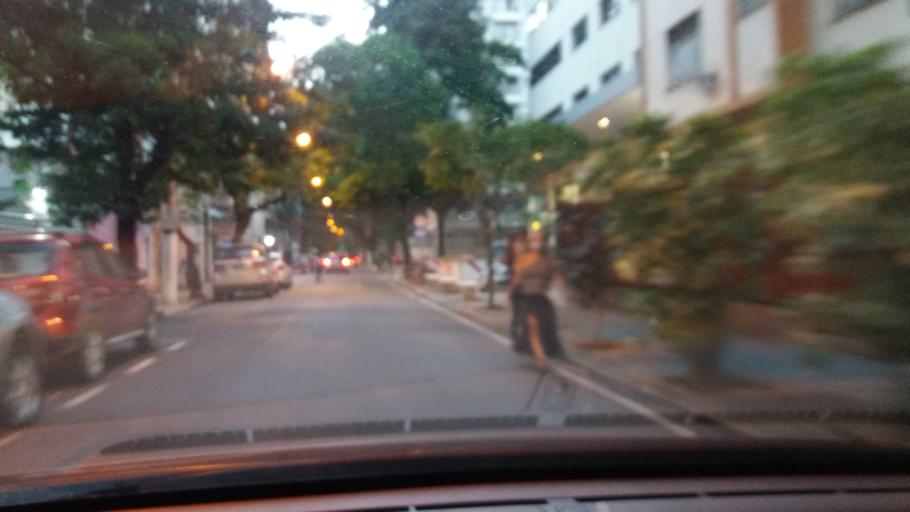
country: BR
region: Rio de Janeiro
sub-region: Niteroi
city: Niteroi
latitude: -22.9024
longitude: -43.1036
